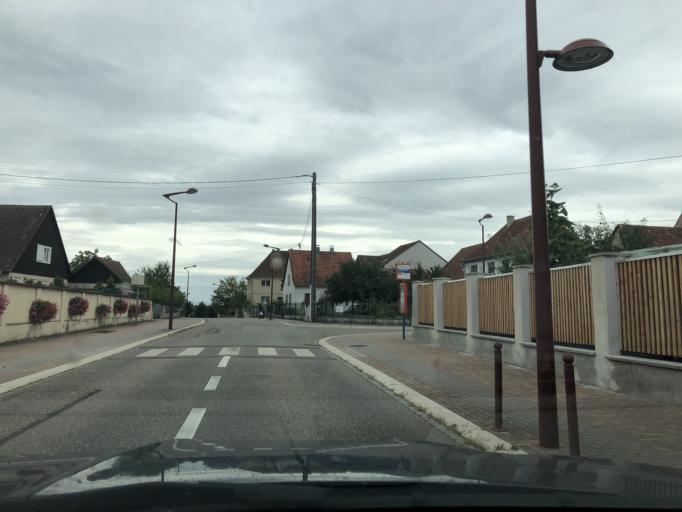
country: DE
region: Rheinland-Pfalz
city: Berg
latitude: 48.9735
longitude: 8.1848
